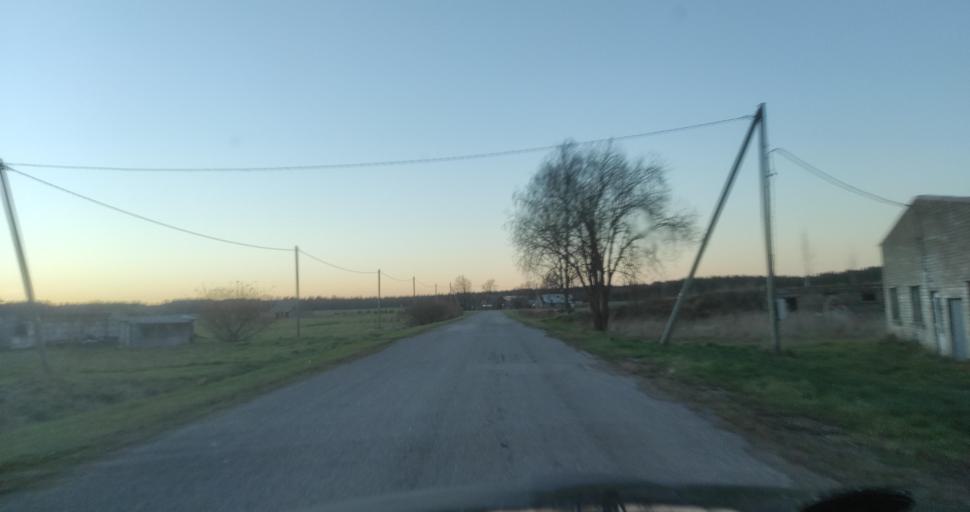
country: LV
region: Dundaga
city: Dundaga
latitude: 57.3760
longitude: 22.2280
